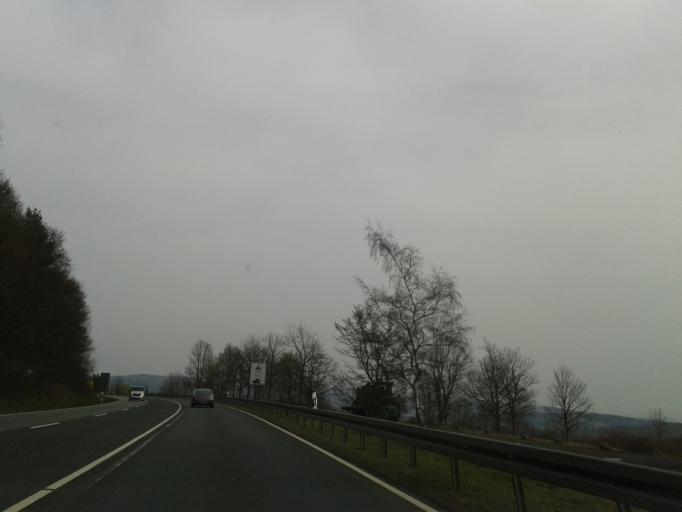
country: DE
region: Hesse
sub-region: Regierungsbezirk Giessen
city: Merkenbach
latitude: 50.6744
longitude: 8.2565
